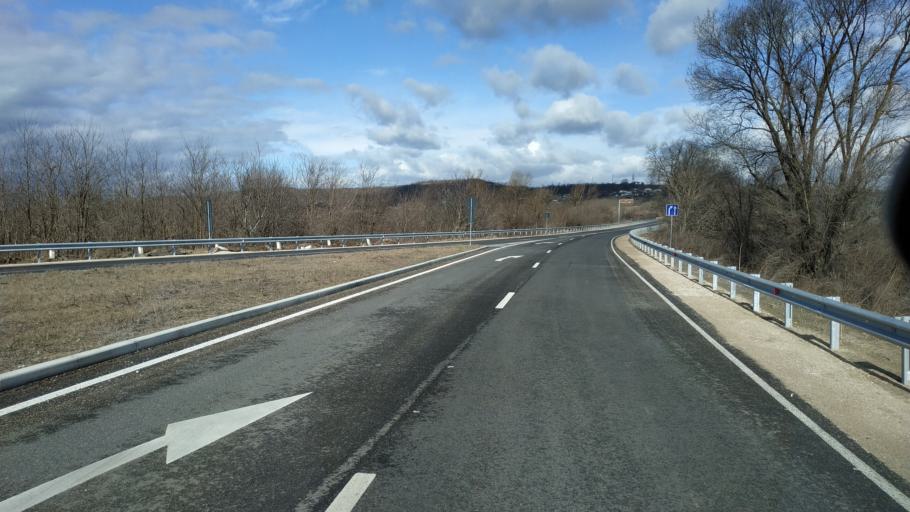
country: MD
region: Stinga Nistrului
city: Bucovat
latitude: 47.1810
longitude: 28.4675
